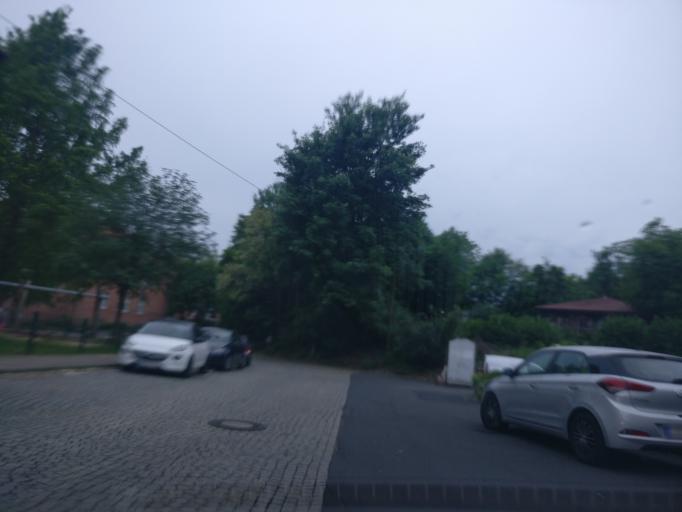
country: DE
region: Lower Saxony
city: Hannoversch Munden
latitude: 51.4061
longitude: 9.6378
